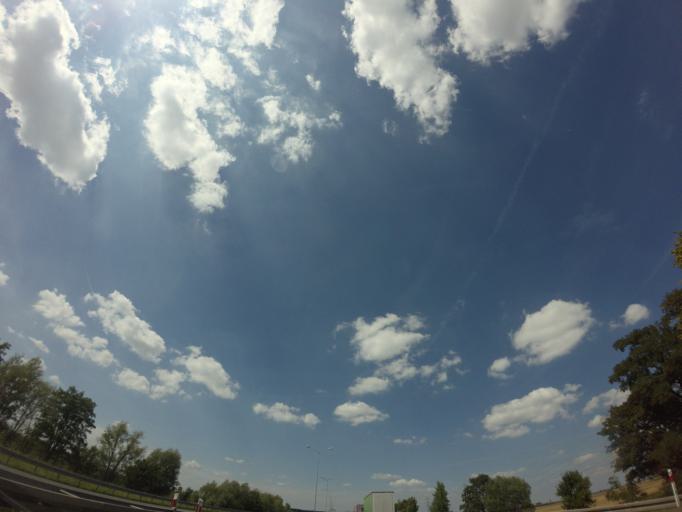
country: PL
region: Lower Silesian Voivodeship
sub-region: Powiat strzelinski
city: Wiazow
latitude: 50.8719
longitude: 17.2117
